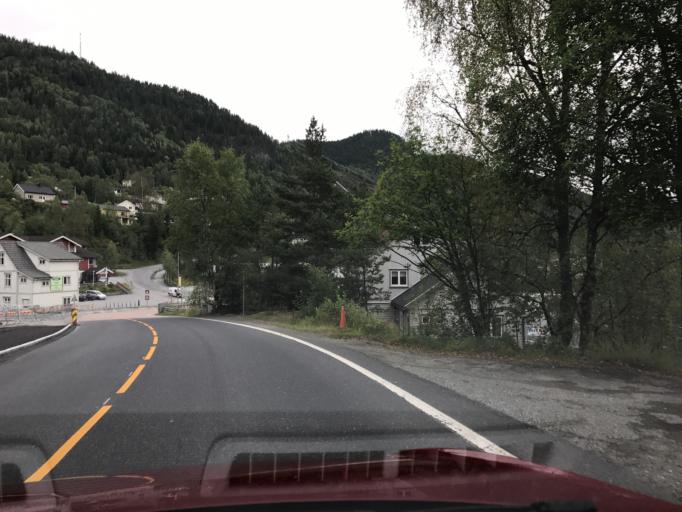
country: NO
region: Buskerud
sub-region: Nore og Uvdal
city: Rodberg
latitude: 60.2669
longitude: 8.9411
